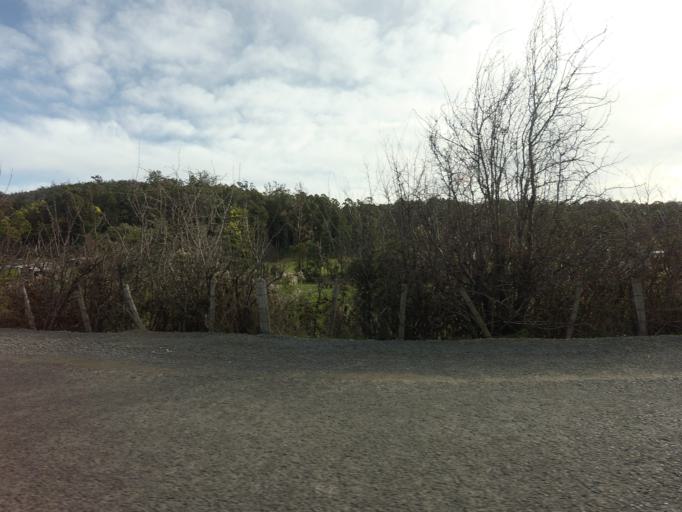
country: AU
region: Tasmania
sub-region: Kingborough
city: Margate
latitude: -42.9893
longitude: 147.1898
